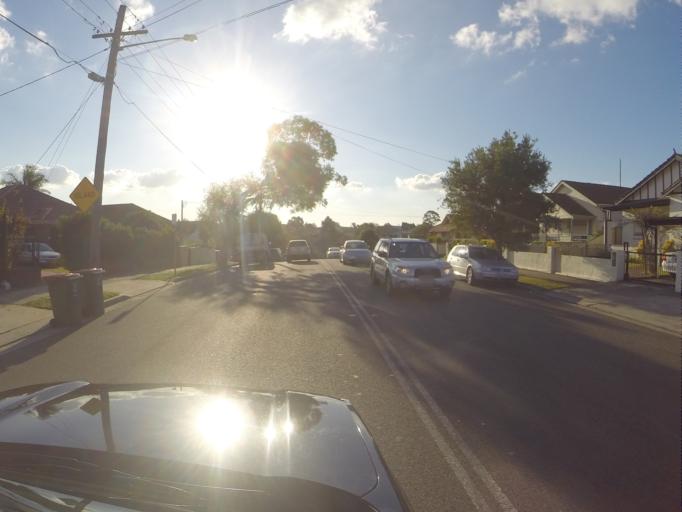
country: AU
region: New South Wales
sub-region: Rockdale
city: Bexley
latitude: -33.9488
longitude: 151.1142
